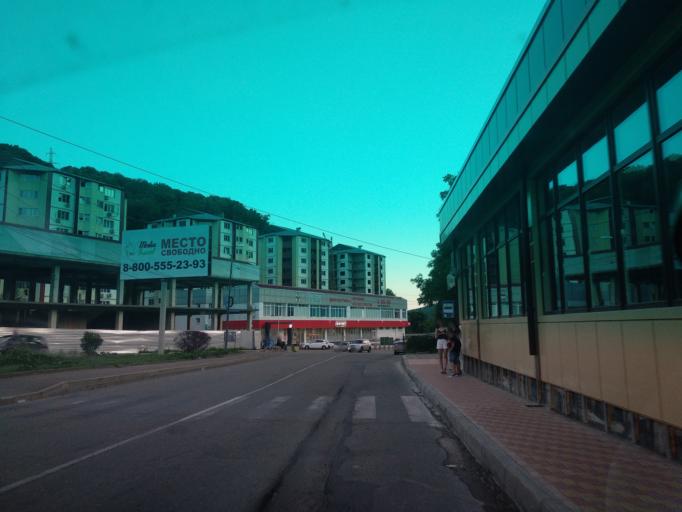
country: RU
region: Krasnodarskiy
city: Tuapse
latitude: 44.1224
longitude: 39.0726
